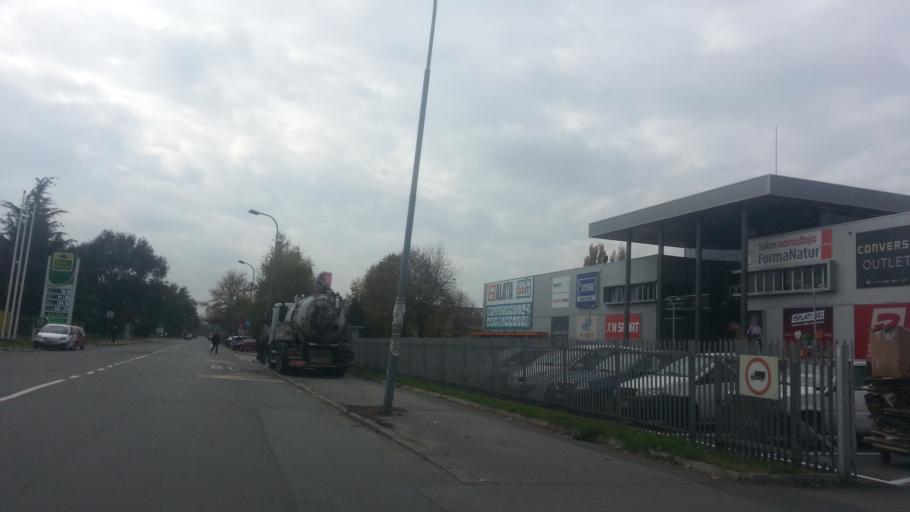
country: RS
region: Central Serbia
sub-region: Belgrade
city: Zemun
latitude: 44.8626
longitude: 20.3683
